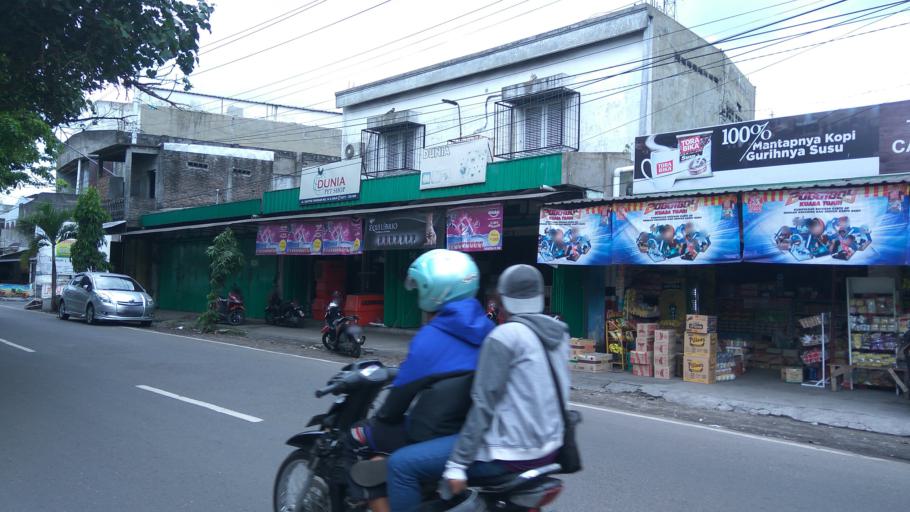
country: ID
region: Central Java
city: Surakarta
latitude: -7.5504
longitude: 110.8217
